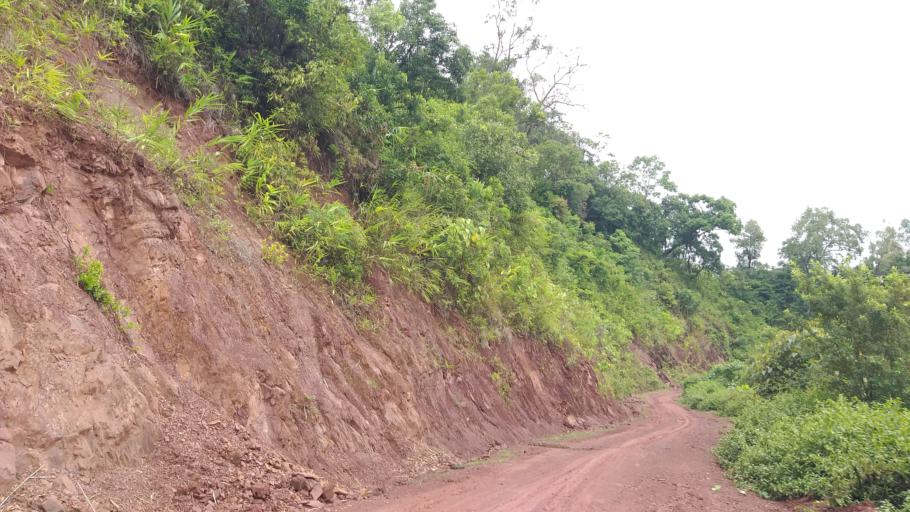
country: LA
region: Phongsali
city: Khoa
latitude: 21.3638
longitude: 102.6107
